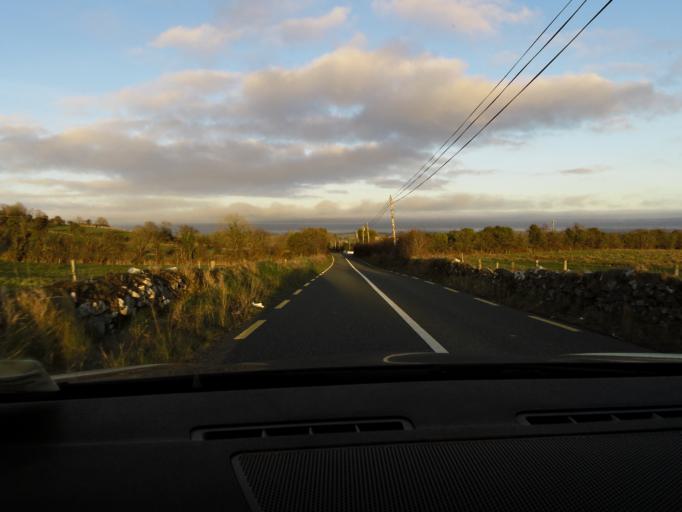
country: IE
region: Connaught
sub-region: Sligo
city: Tobercurry
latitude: 54.0442
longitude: -8.6707
